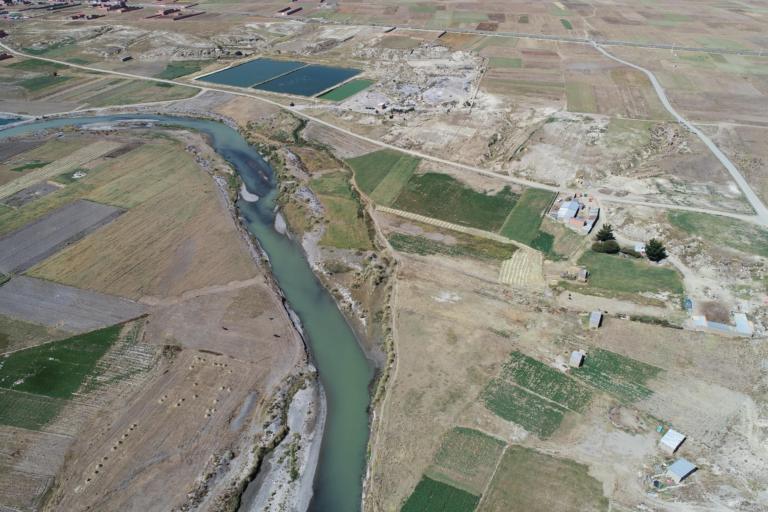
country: BO
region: La Paz
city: Achacachi
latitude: -16.0385
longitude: -68.7013
